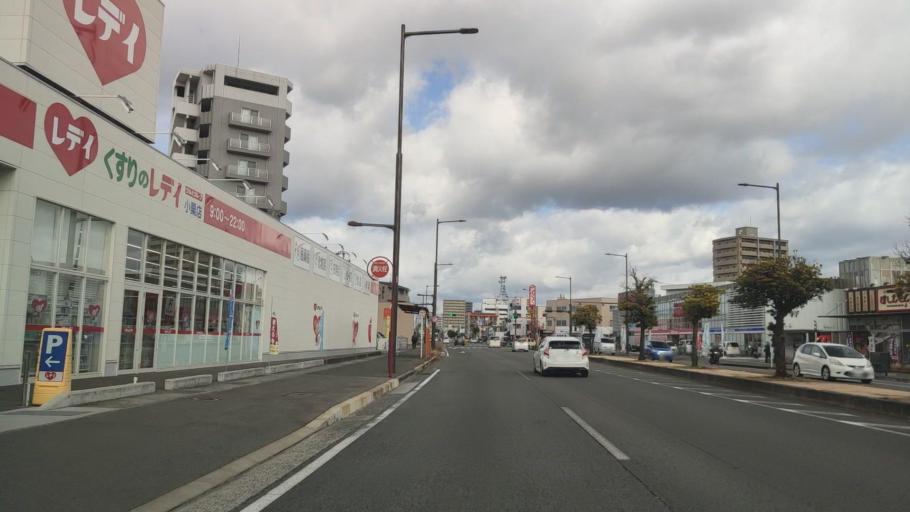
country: JP
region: Ehime
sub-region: Shikoku-chuo Shi
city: Matsuyama
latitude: 33.8269
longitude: 132.7588
